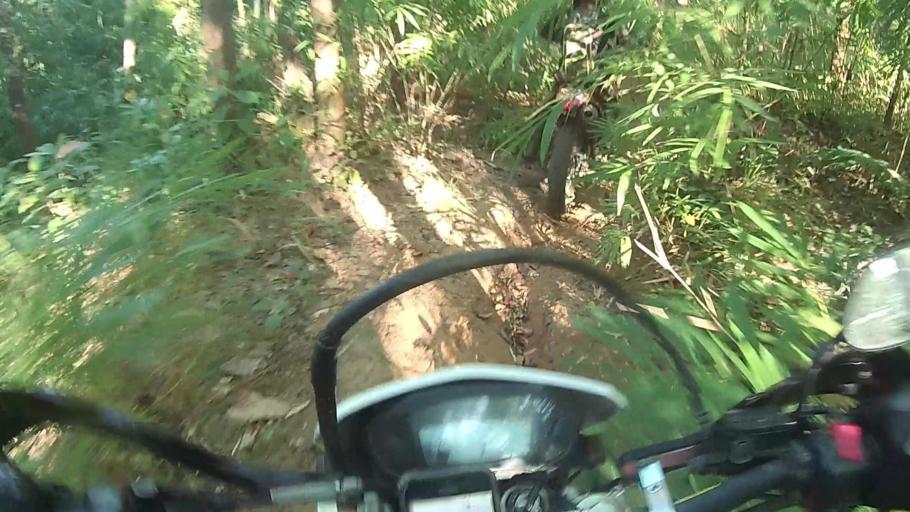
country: TH
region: Chiang Mai
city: Mae Taeng
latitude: 18.9560
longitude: 98.8736
